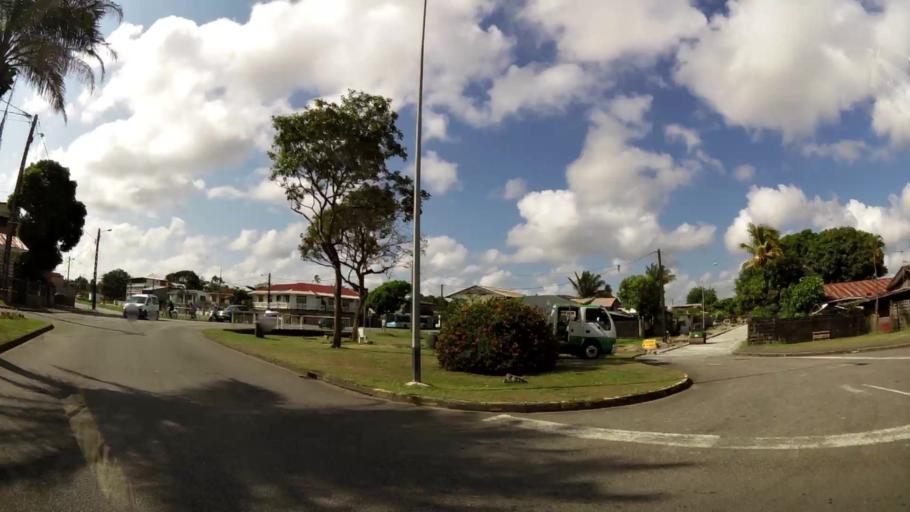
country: GF
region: Guyane
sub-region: Guyane
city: Cayenne
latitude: 4.9354
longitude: -52.3193
